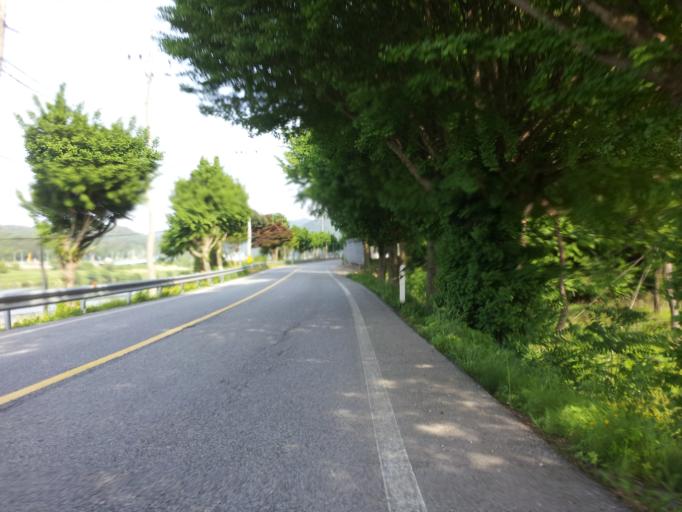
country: KR
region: Chungcheongnam-do
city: Gongju
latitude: 36.4425
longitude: 127.1909
